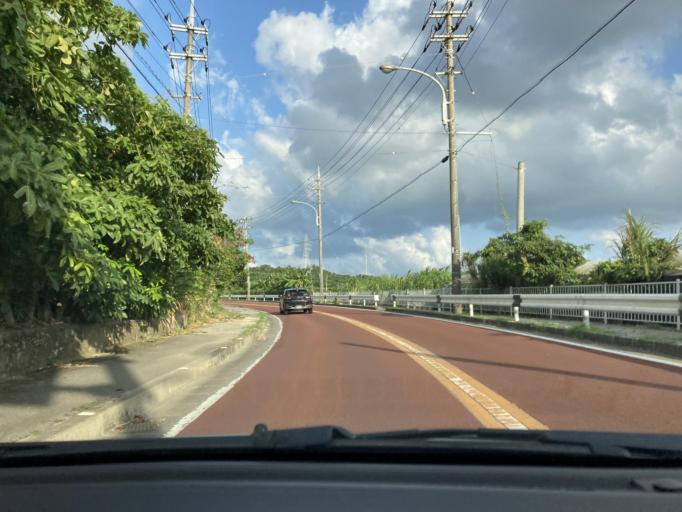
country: JP
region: Okinawa
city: Itoman
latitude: 26.1338
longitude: 127.6901
